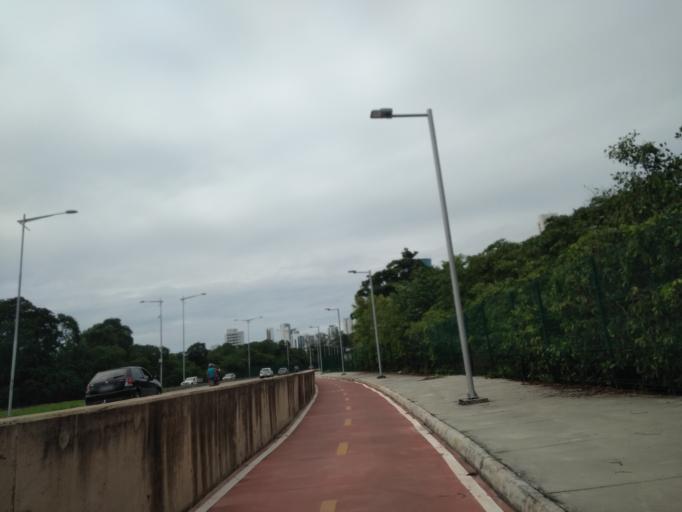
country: BR
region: Pernambuco
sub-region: Recife
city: Recife
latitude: -8.1054
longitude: -34.8914
